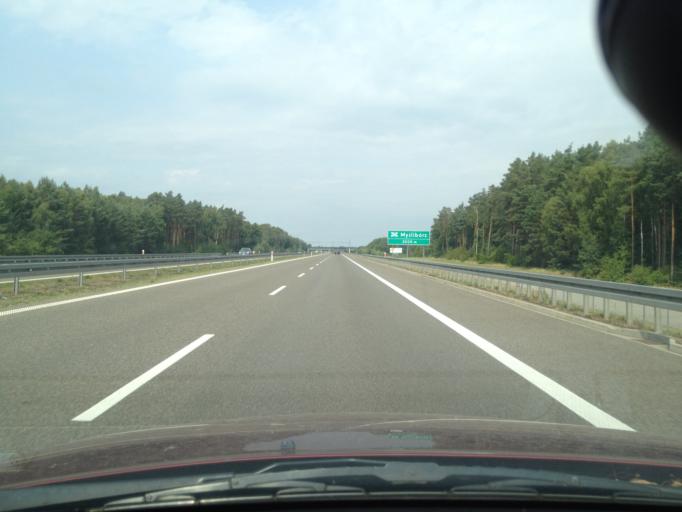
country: PL
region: West Pomeranian Voivodeship
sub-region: Powiat mysliborski
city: Nowogrodek Pomorski
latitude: 52.9319
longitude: 14.9848
